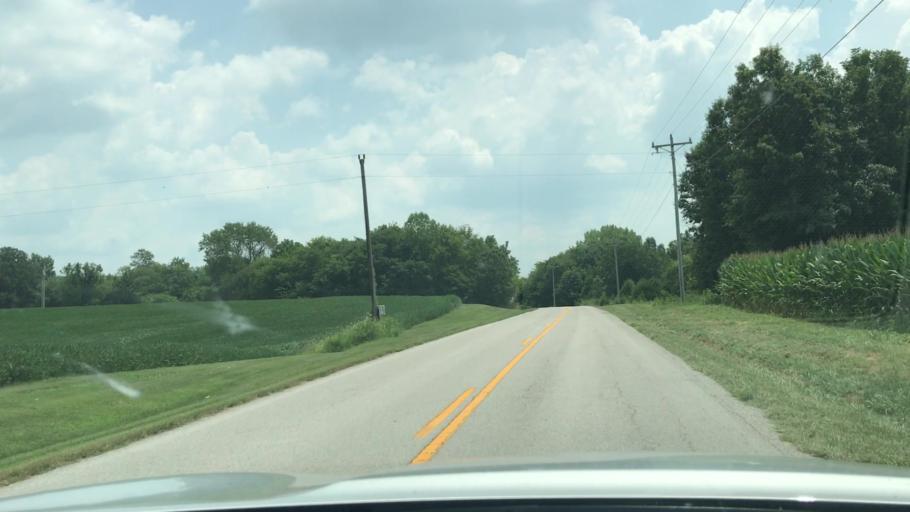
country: US
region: Kentucky
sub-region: Todd County
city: Elkton
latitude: 36.7623
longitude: -87.1054
